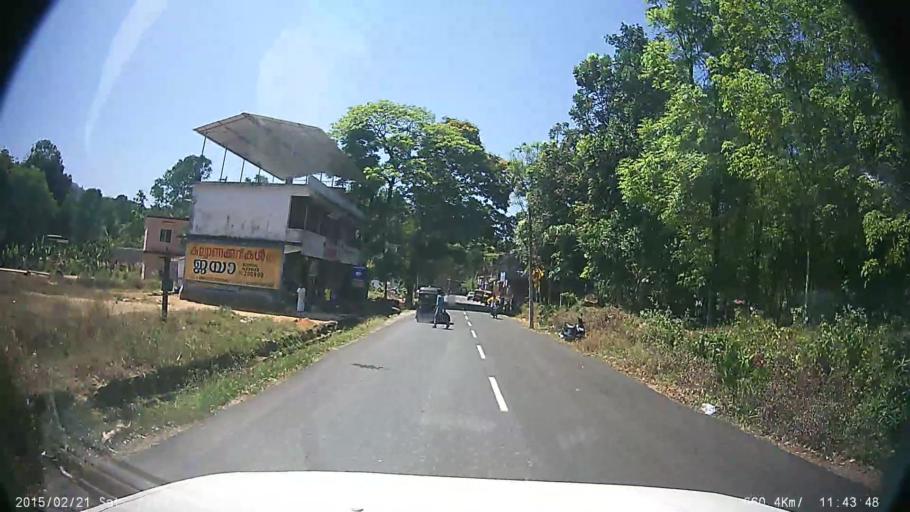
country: IN
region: Kerala
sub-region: Kottayam
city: Lalam
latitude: 9.7800
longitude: 76.7300
